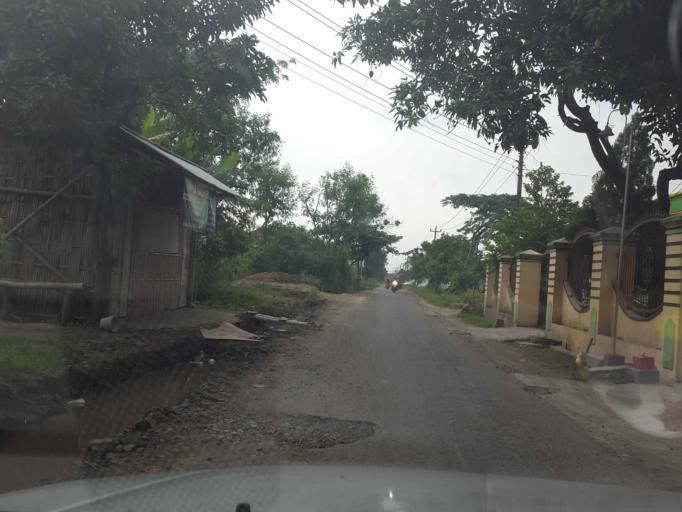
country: ID
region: Central Java
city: Jaten
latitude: -7.5547
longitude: 110.8979
